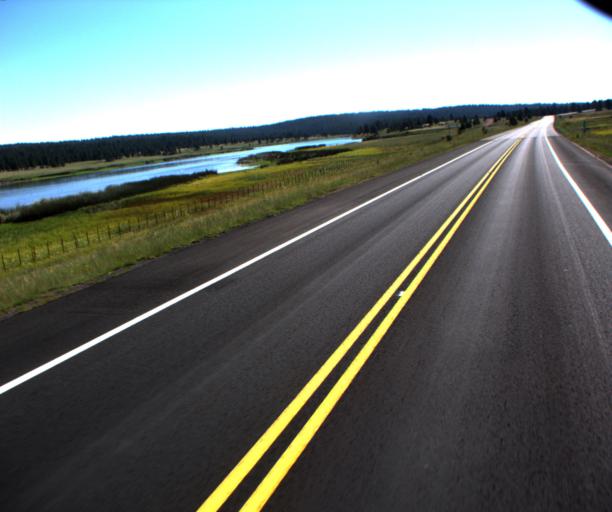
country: US
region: Arizona
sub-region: Apache County
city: Eagar
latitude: 33.8274
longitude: -109.0955
